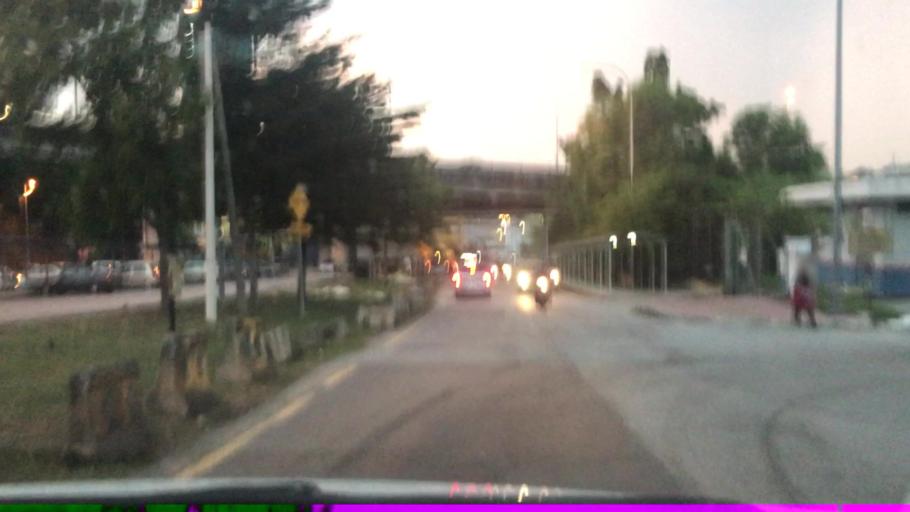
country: MY
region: Selangor
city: Kampong Baharu Balakong
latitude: 3.0769
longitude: 101.7137
